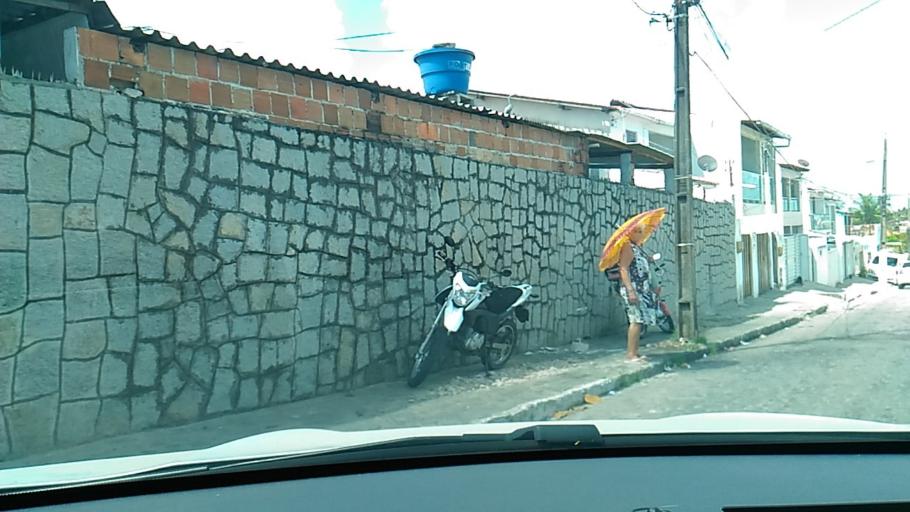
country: BR
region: Paraiba
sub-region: Joao Pessoa
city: Joao Pessoa
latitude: -7.1640
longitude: -34.8422
